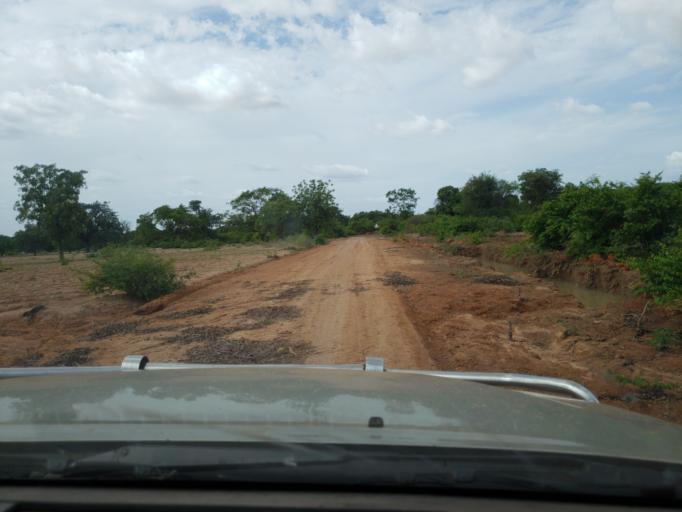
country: ML
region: Segou
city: Bla
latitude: 12.7183
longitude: -5.6822
